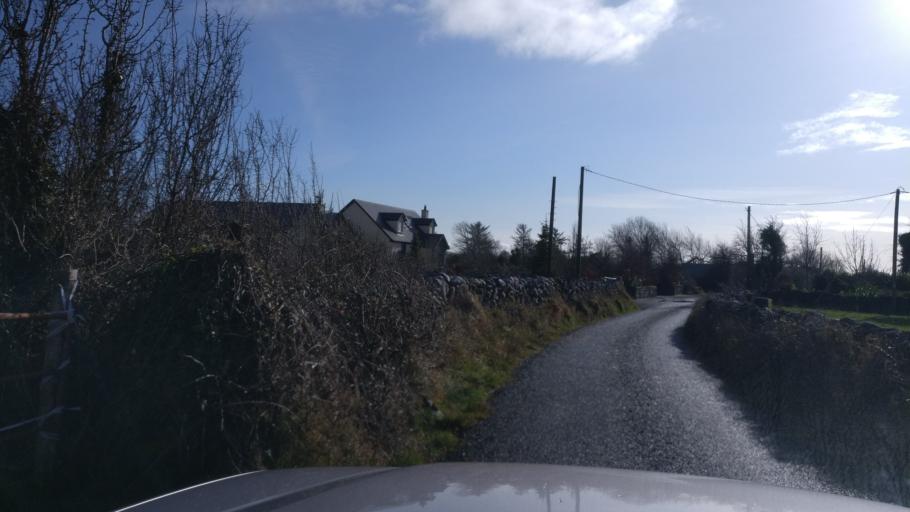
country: IE
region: Connaught
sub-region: County Galway
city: Athenry
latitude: 53.2385
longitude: -8.7799
